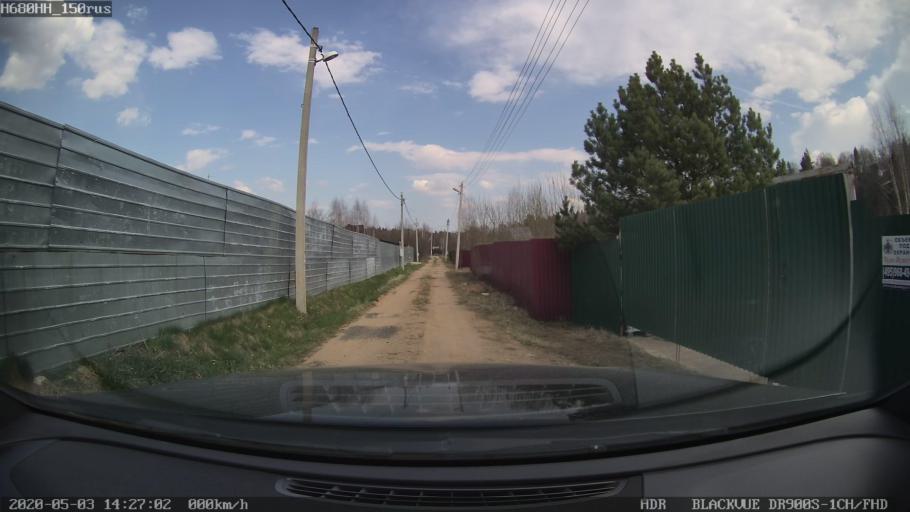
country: RU
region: Moskovskaya
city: Solnechnogorsk
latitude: 56.2510
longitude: 37.0079
